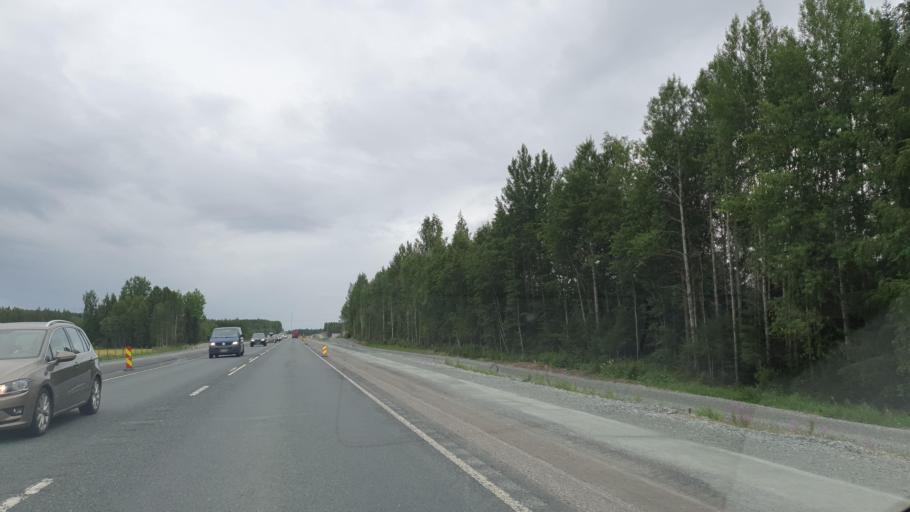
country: FI
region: Northern Savo
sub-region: Ylae-Savo
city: Lapinlahti
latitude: 63.2947
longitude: 27.4531
